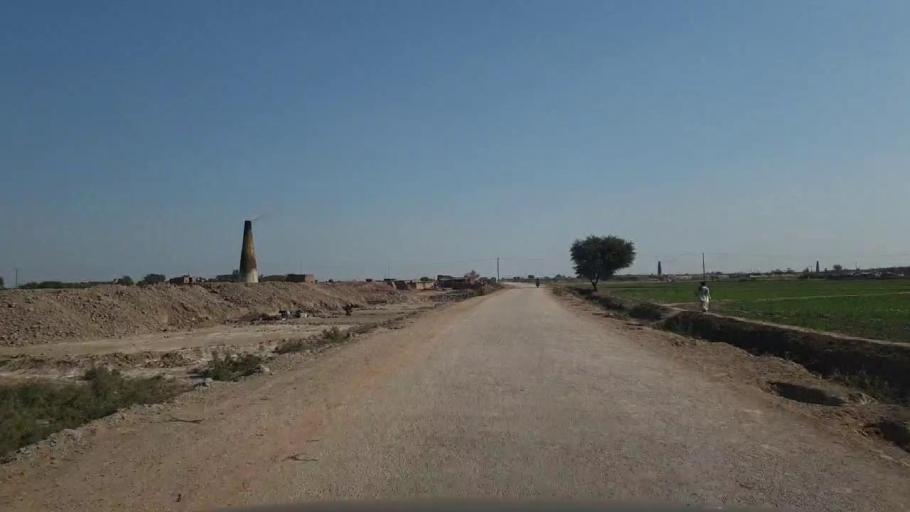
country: PK
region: Sindh
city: Tando Allahyar
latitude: 25.4140
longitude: 68.7004
